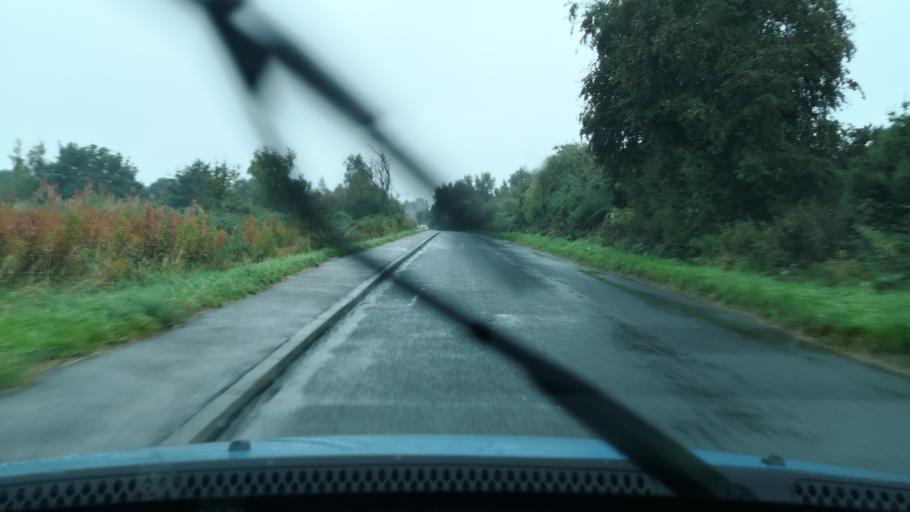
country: GB
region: England
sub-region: City and Borough of Wakefield
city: Sharlston
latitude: 53.6694
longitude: -1.4066
